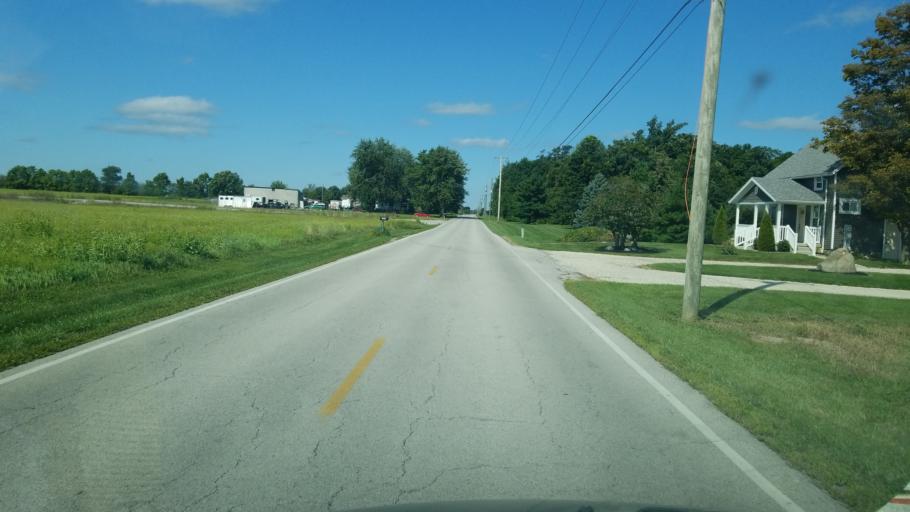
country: US
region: Ohio
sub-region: Hancock County
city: Findlay
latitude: 41.1091
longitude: -83.5792
